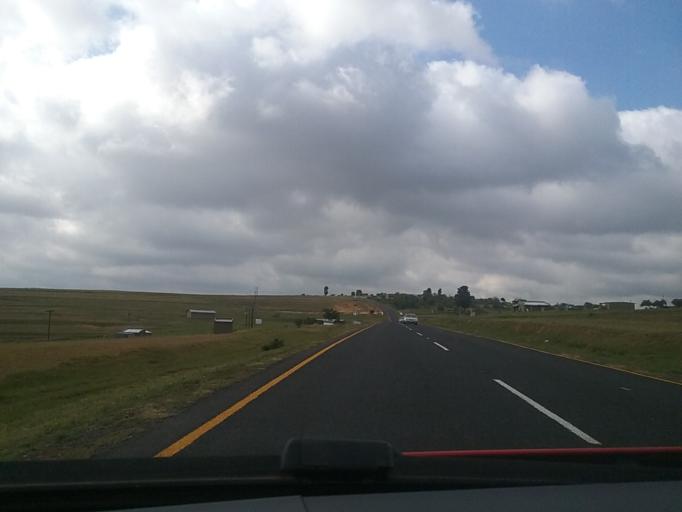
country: LS
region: Berea
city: Teyateyaneng
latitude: -29.1898
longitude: 27.8043
